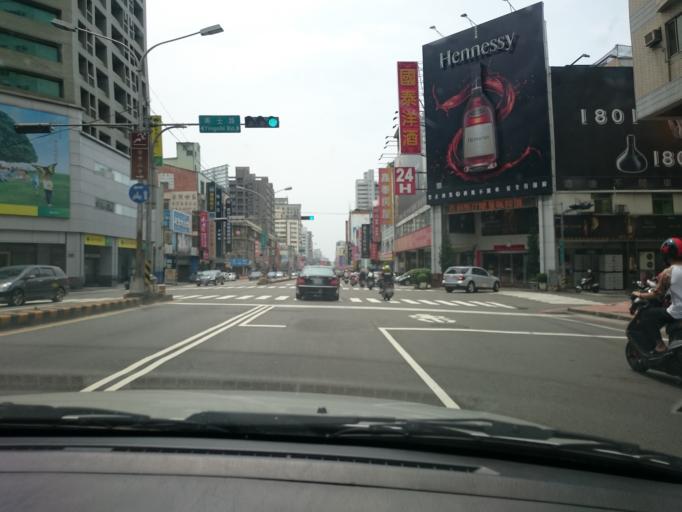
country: TW
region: Taiwan
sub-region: Taichung City
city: Taichung
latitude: 24.1506
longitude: 120.6765
